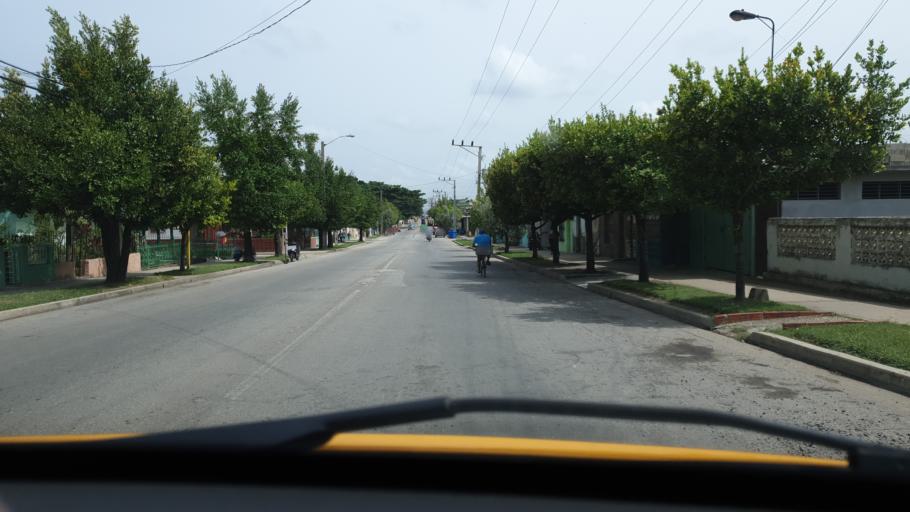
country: CU
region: Villa Clara
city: Santa Clara
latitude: 22.3918
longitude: -79.9608
